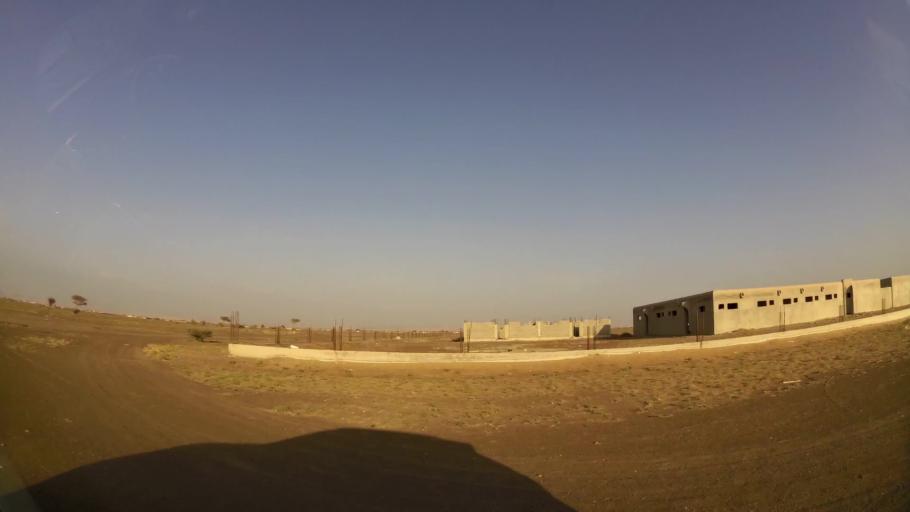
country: AE
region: Abu Dhabi
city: Al Ain
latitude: 24.1448
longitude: 55.8452
